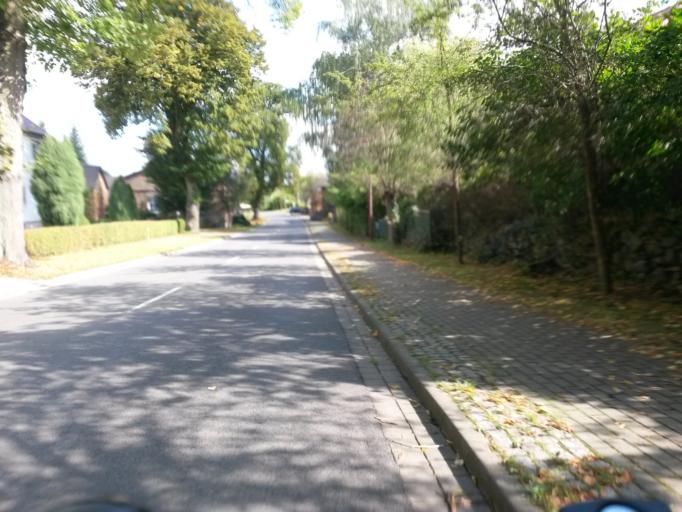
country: DE
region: Brandenburg
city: Templin
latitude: 53.2040
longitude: 13.5595
